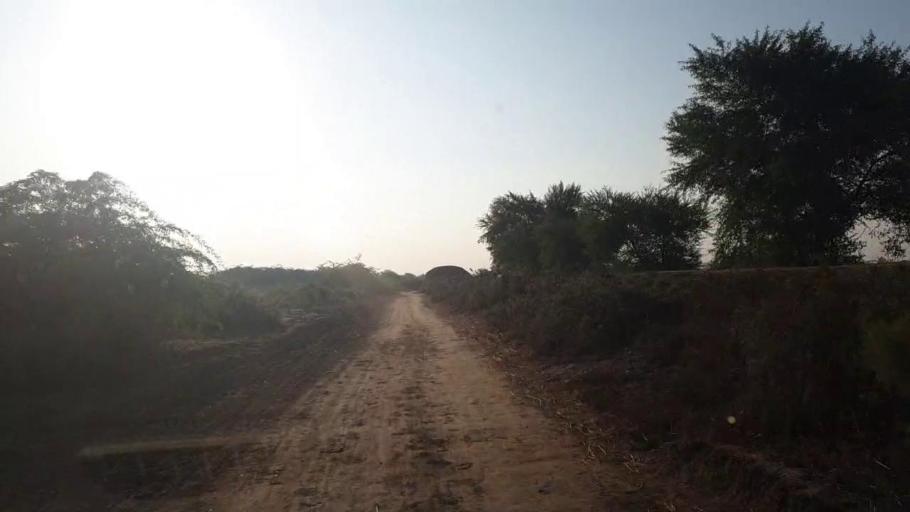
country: PK
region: Sindh
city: Badin
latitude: 24.6363
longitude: 68.7932
